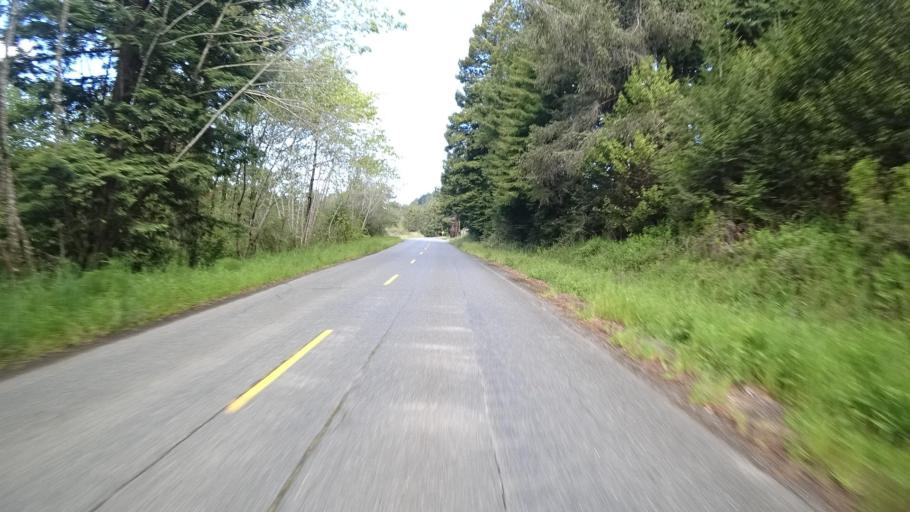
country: US
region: California
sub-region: Humboldt County
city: Blue Lake
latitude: 40.9052
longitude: -124.0336
